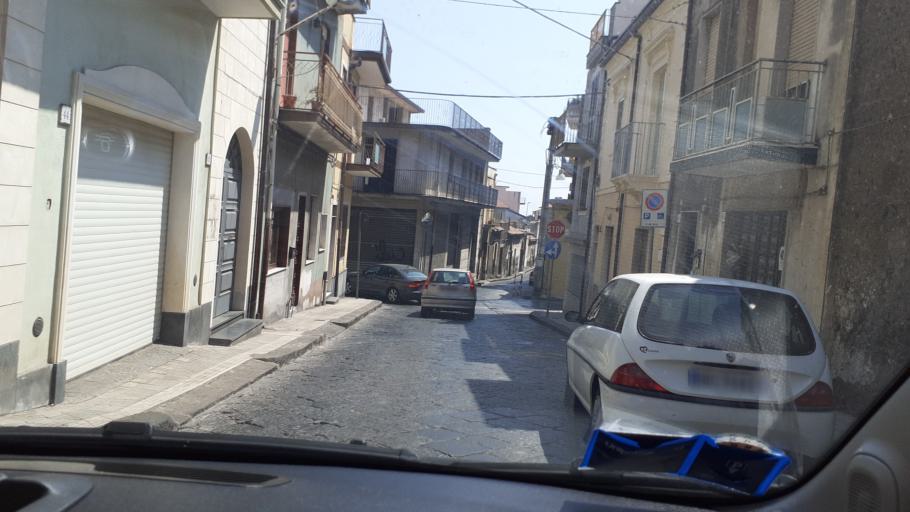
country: IT
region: Sicily
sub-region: Catania
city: Misterbianco
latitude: 37.5185
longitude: 15.0123
